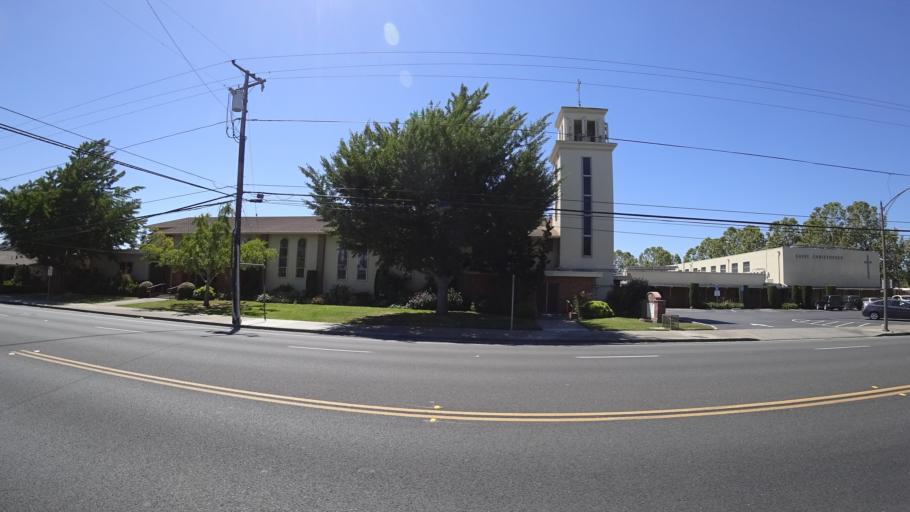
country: US
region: California
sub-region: Santa Clara County
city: Cambrian Park
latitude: 37.2843
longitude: -121.9034
